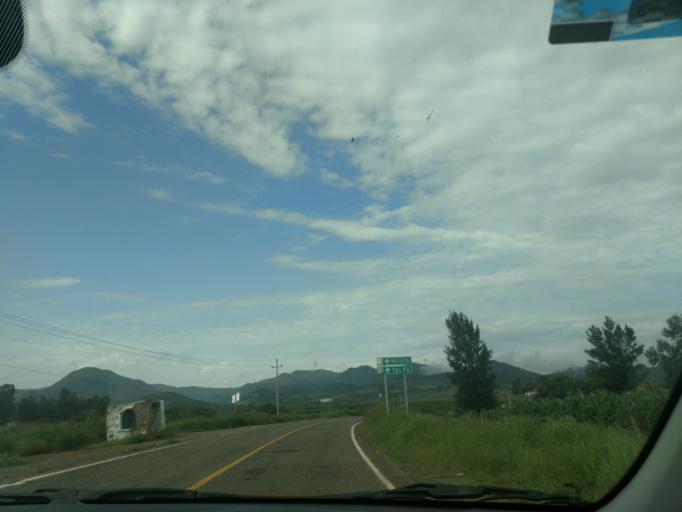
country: MX
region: Jalisco
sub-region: Atengo
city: Soyatlan del Oro
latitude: 20.5298
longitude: -104.3208
